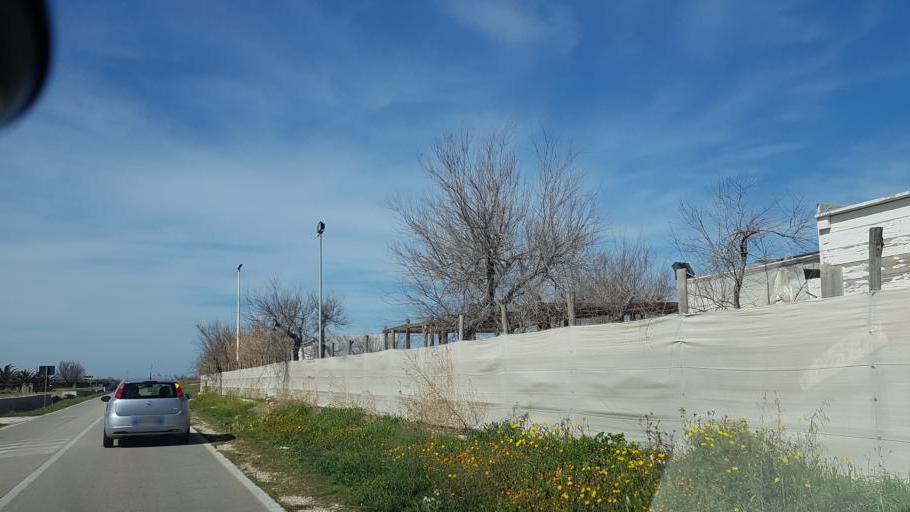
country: IT
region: Apulia
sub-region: Provincia di Brindisi
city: Pezze di Greco
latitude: 40.8446
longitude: 17.4621
